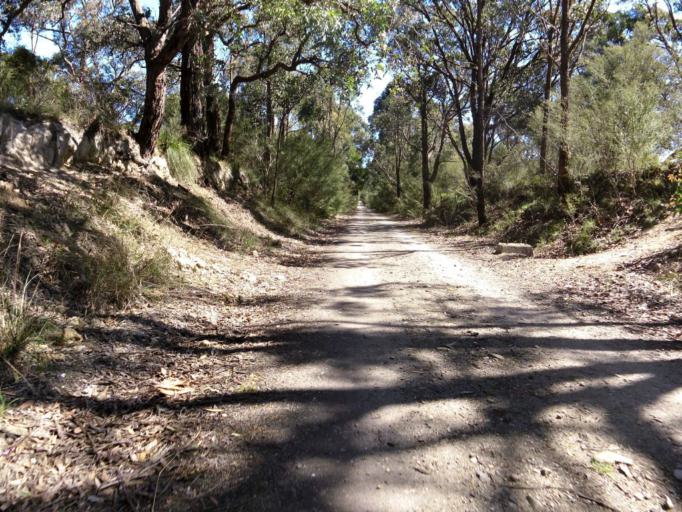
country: AU
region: Victoria
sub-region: Latrobe
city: Moe
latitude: -38.1716
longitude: 146.2951
